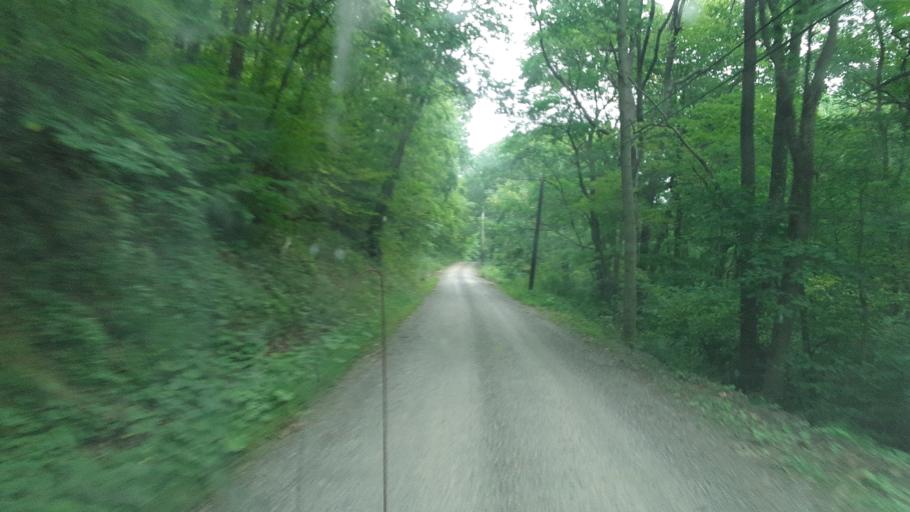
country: US
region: Pennsylvania
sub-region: Jefferson County
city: Punxsutawney
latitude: 40.9643
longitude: -79.1236
